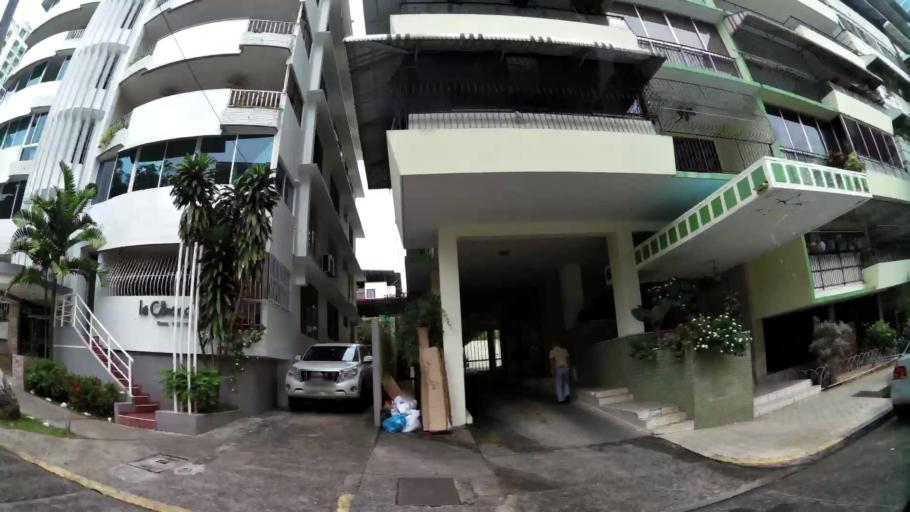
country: PA
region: Panama
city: Panama
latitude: 8.9860
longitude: -79.5305
